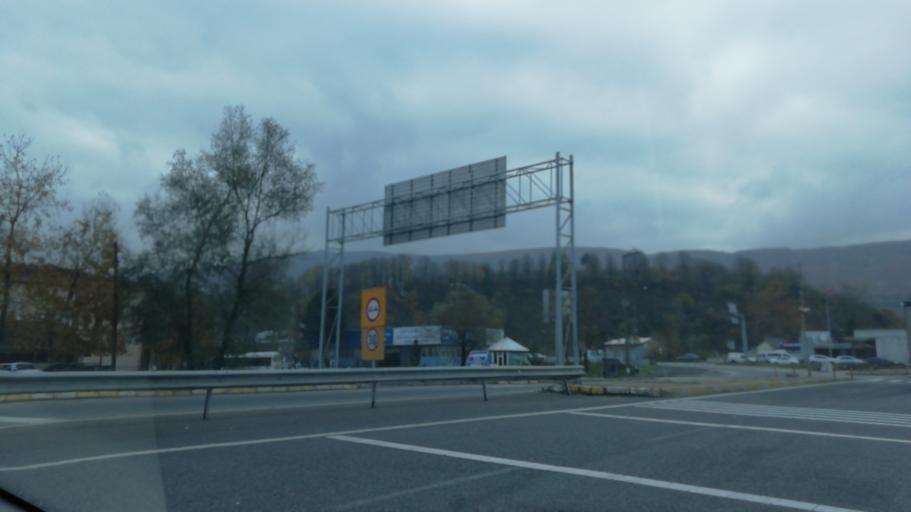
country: TR
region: Duzce
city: Kaynasli
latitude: 40.7831
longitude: 31.2778
